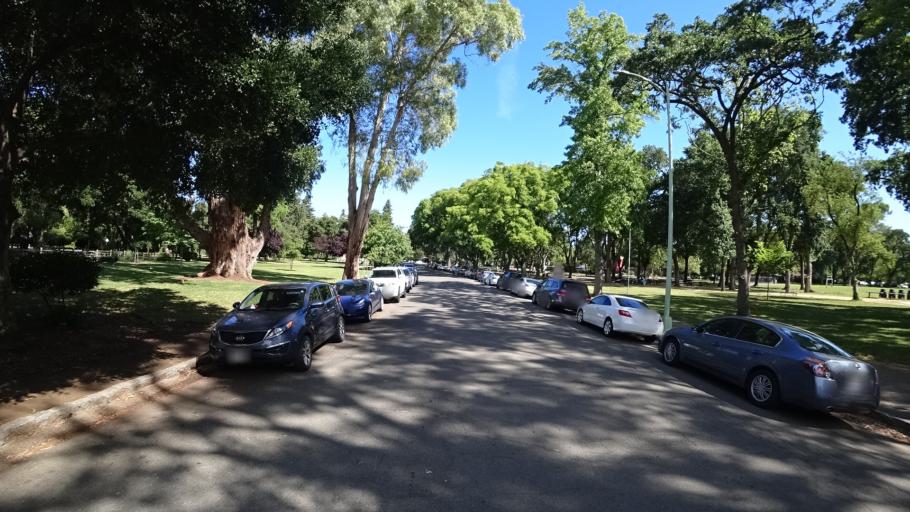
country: US
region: California
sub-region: Sacramento County
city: Sacramento
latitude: 38.5380
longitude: -121.5017
